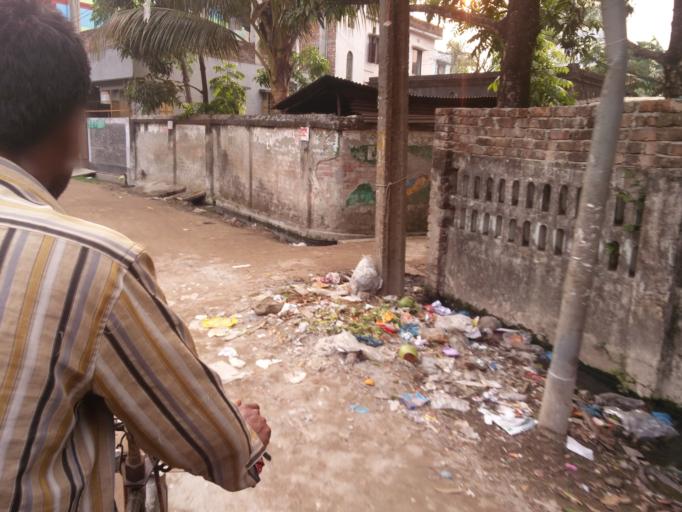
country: BD
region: Dhaka
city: Mymensingh
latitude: 24.7567
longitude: 90.3952
